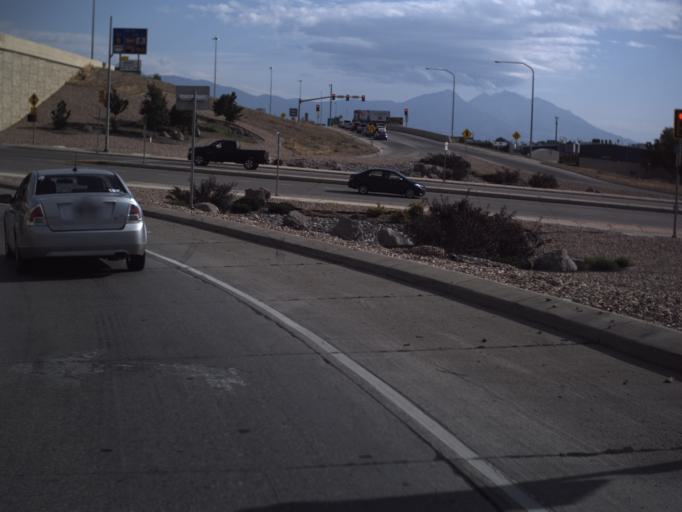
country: US
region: Utah
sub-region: Utah County
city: Lindon
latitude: 40.3126
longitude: -111.7269
